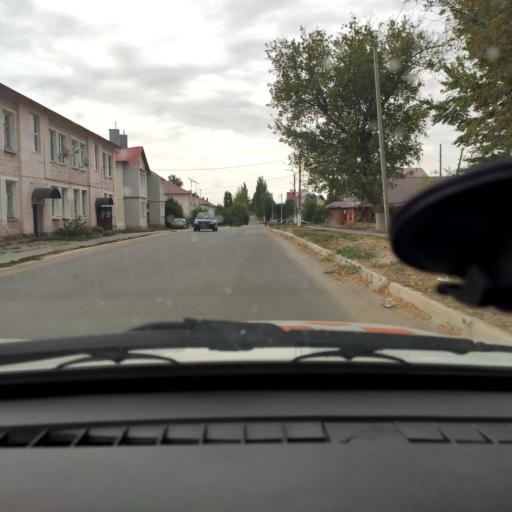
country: RU
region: Voronezj
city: Strelitsa
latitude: 51.6117
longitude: 38.9021
